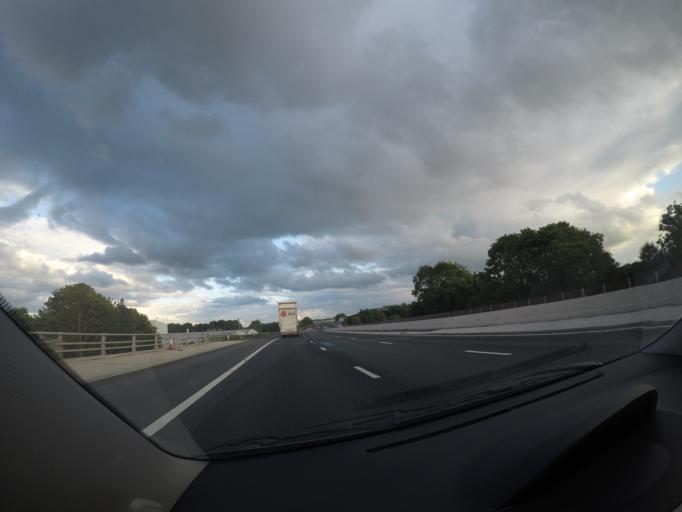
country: GB
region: England
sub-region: North Yorkshire
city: Catterick
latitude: 54.3915
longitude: -1.6574
